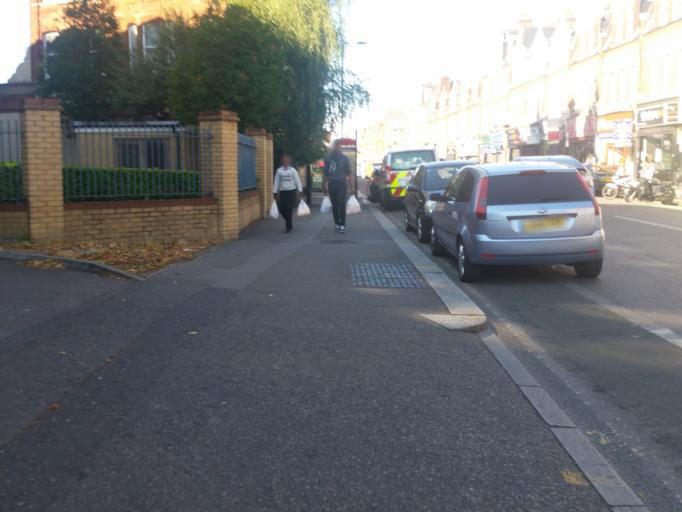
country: GB
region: England
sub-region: Greater London
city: Crouch End
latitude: 51.5835
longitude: -0.1166
